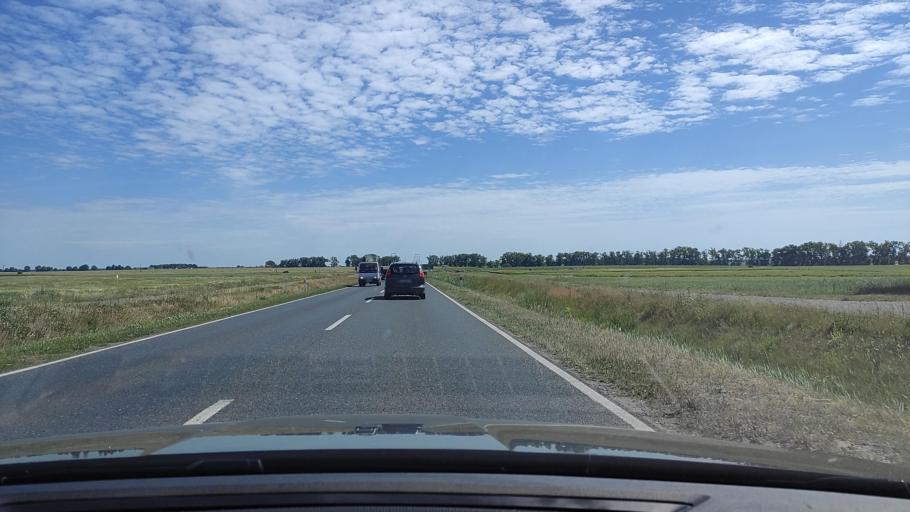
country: PL
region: Greater Poland Voivodeship
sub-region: Powiat poznanski
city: Murowana Goslina
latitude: 52.5893
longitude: 17.0007
